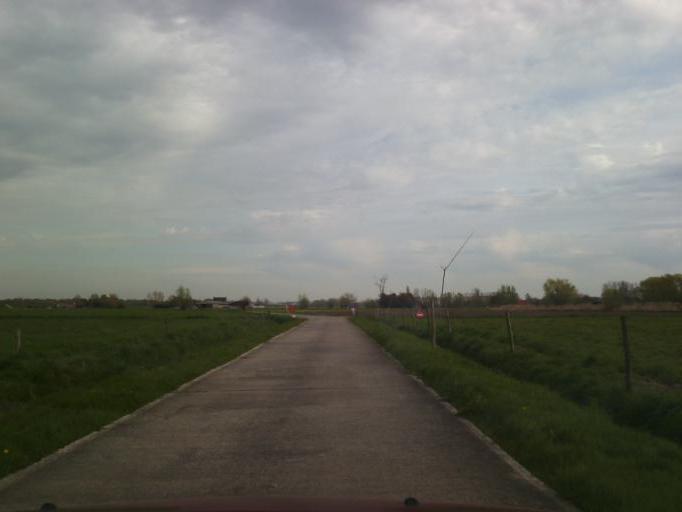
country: BE
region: Flanders
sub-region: Provincie Oost-Vlaanderen
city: Berlare
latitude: 51.0365
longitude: 4.0222
